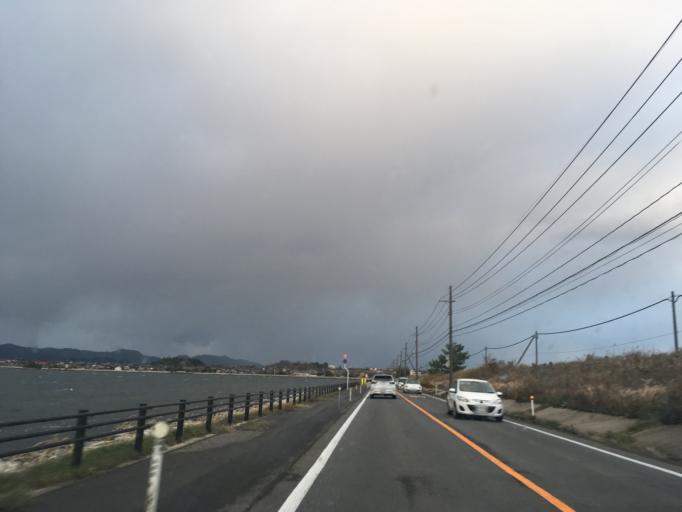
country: JP
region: Shimane
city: Sakaiminato
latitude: 35.4848
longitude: 133.1549
